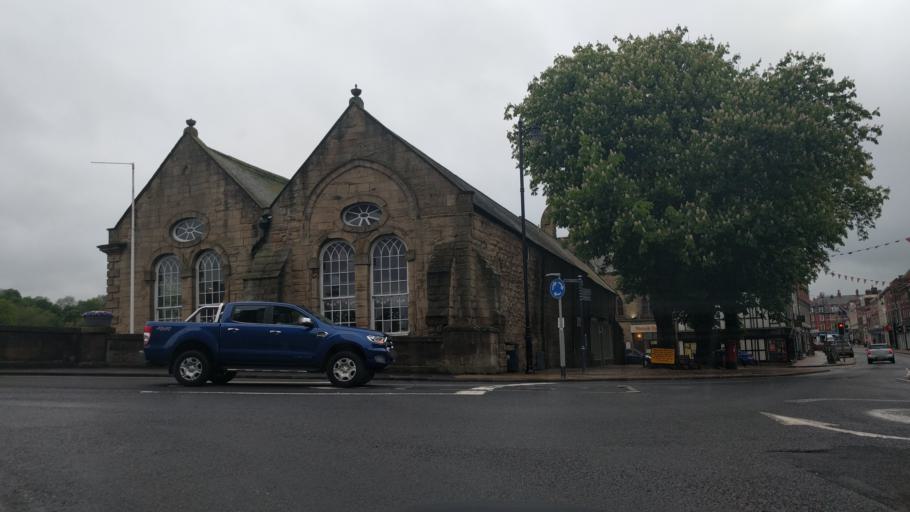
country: GB
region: England
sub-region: Northumberland
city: Morpeth
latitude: 55.1670
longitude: -1.6863
